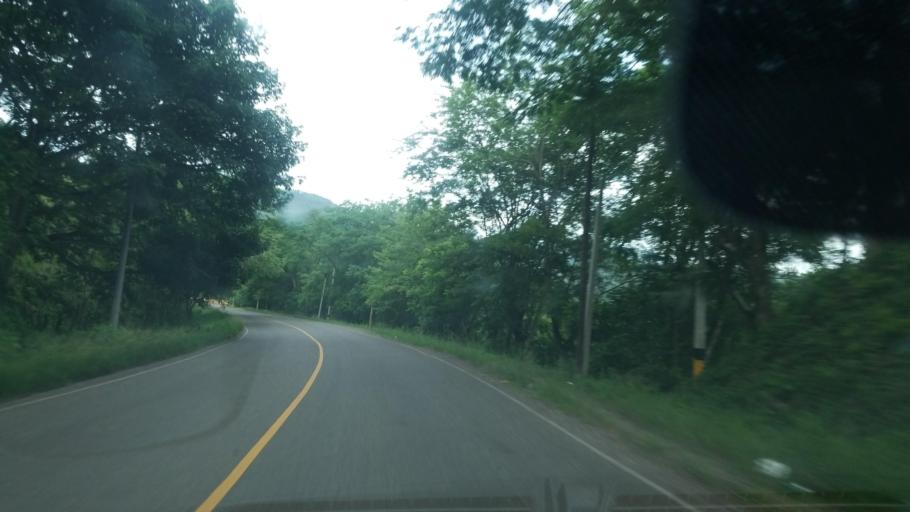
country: HN
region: Santa Barbara
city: Ceguaca
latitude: 14.8121
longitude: -88.1948
